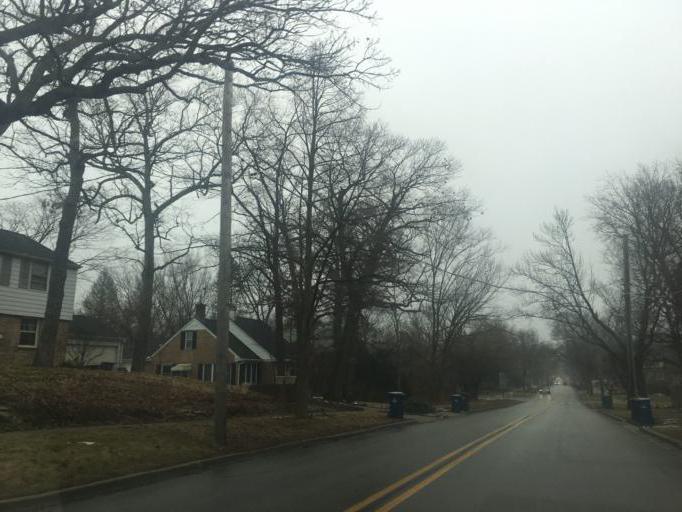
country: US
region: Illinois
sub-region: DuPage County
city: Downers Grove
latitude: 41.7885
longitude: -88.0167
